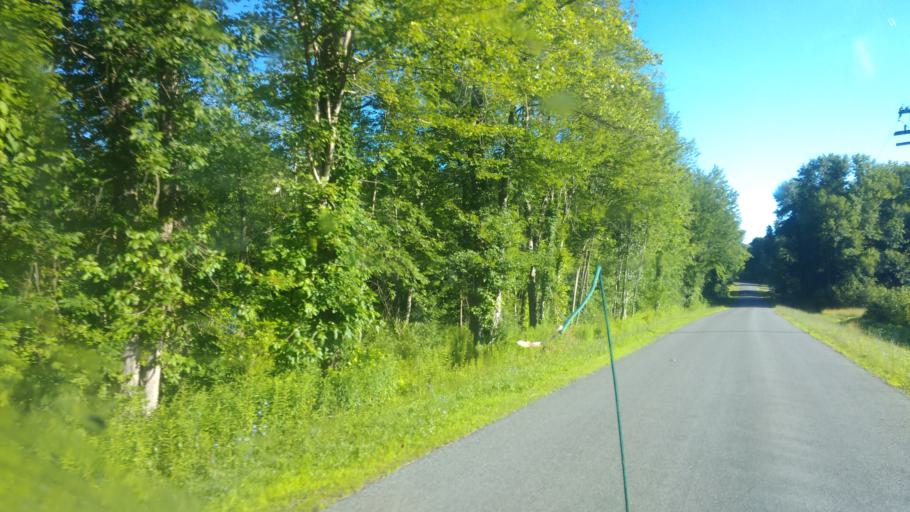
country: US
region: New York
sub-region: Wayne County
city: Sodus
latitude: 43.1468
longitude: -77.0432
